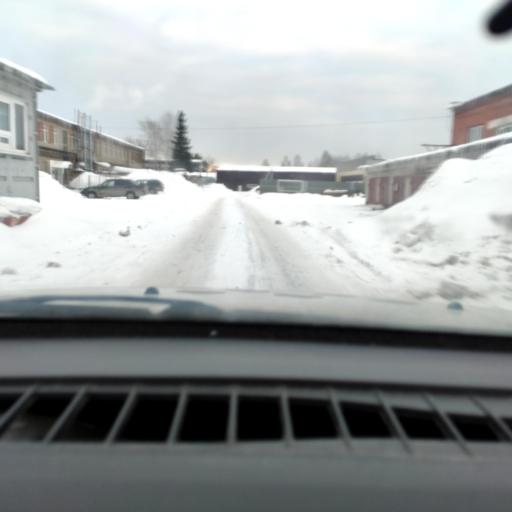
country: RU
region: Perm
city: Perm
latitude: 58.1062
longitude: 56.3497
